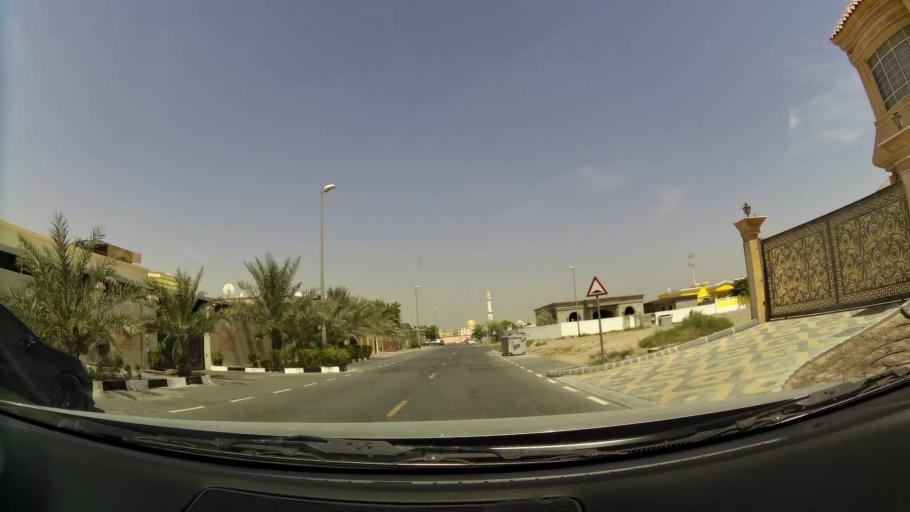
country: AE
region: Ash Shariqah
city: Sharjah
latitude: 25.1876
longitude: 55.4265
